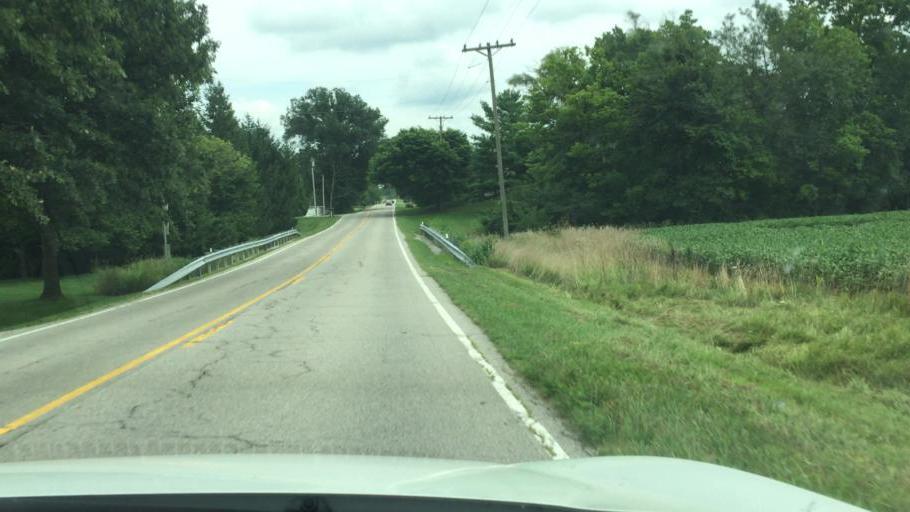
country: US
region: Ohio
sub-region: Champaign County
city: North Lewisburg
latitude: 40.2311
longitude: -83.4629
